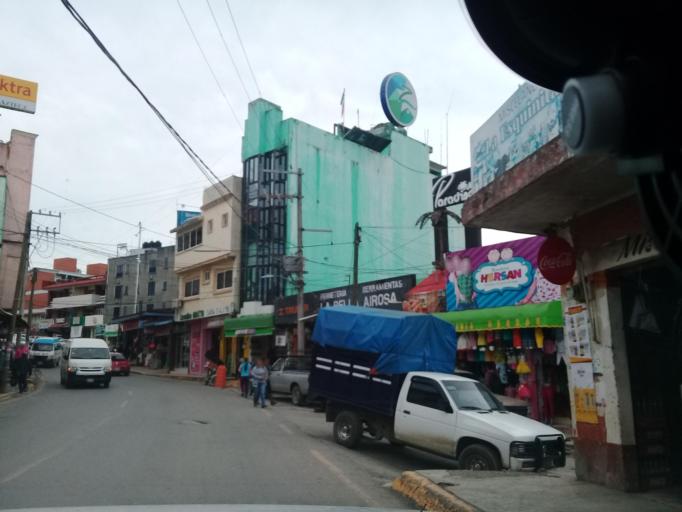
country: MX
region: Hidalgo
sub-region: Huejutla de Reyes
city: Huejutla de Reyes
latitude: 21.1427
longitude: -98.4187
